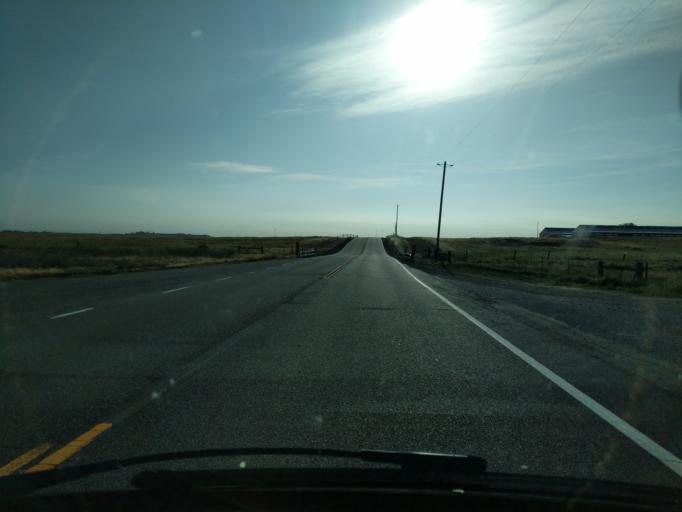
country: US
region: California
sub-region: Stanislaus County
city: East Oakdale
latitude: 37.9373
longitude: -120.8064
